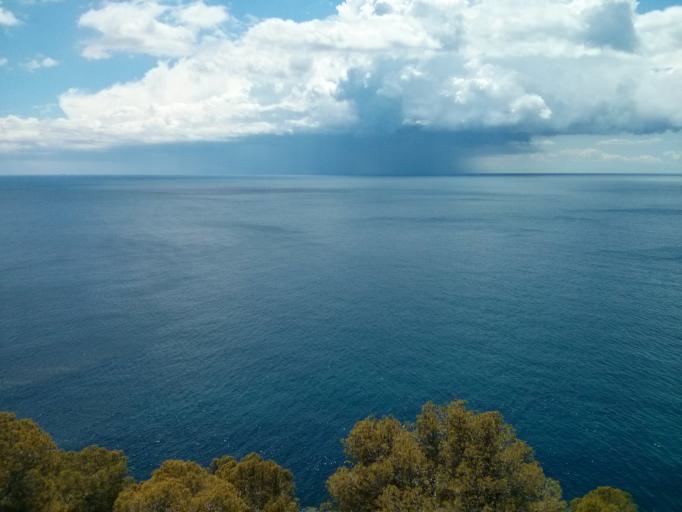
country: ES
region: Valencia
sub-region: Provincia de Alicante
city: Moraira
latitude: 38.7004
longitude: 0.1592
